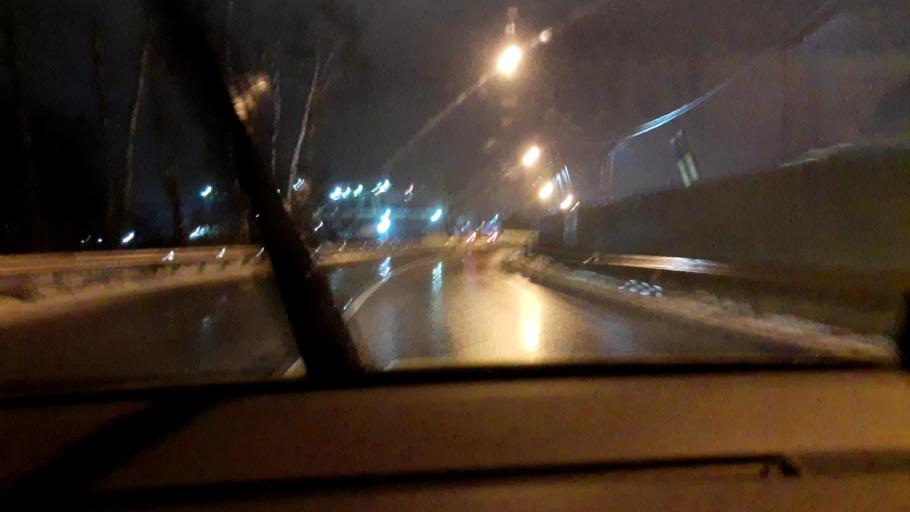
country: RU
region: Moskovskaya
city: Ivanteyevka
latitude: 55.9718
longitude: 37.9186
